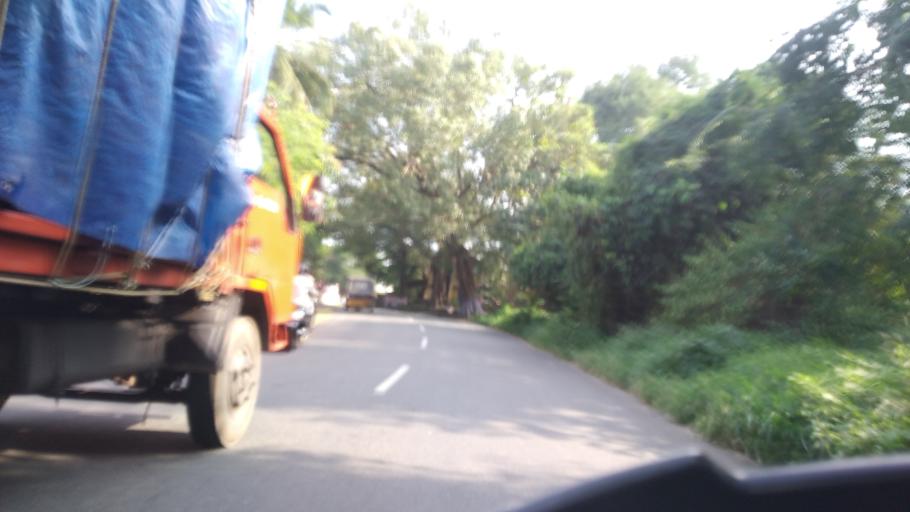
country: IN
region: Kerala
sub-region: Palakkad district
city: Palakkad
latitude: 10.6007
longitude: 76.5501
